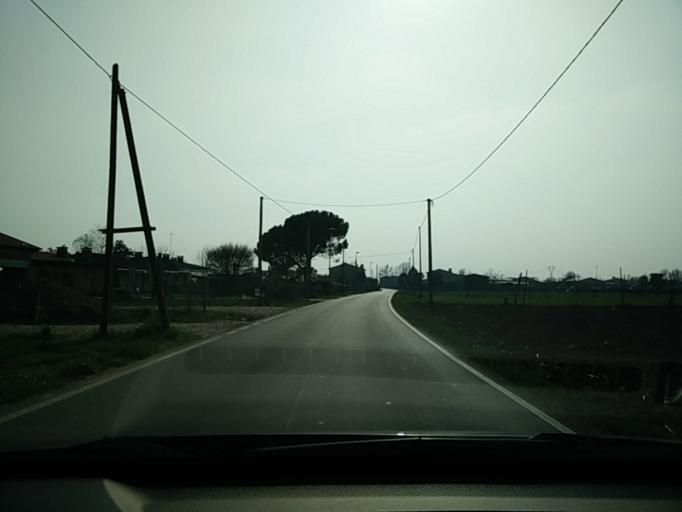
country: IT
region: Veneto
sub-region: Provincia di Treviso
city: Volpago del Montello
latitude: 45.7684
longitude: 12.1341
